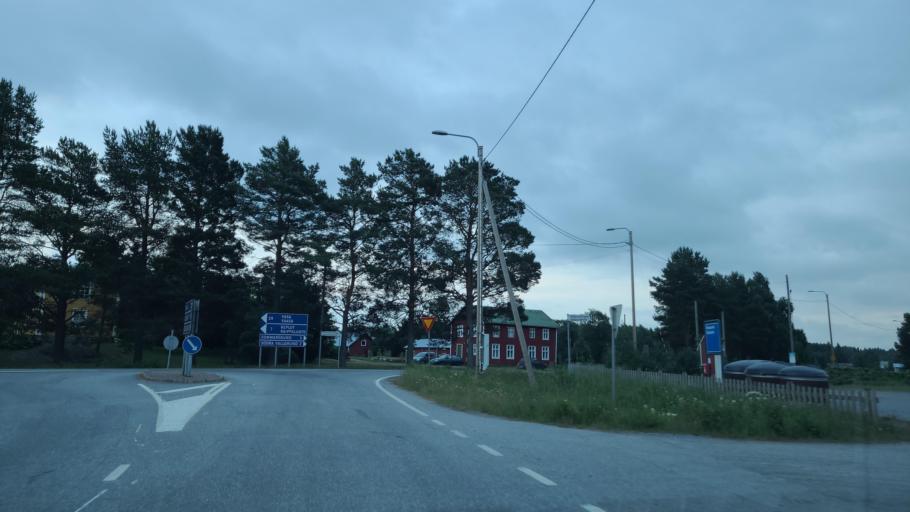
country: FI
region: Ostrobothnia
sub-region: Vaasa
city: Replot
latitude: 63.1962
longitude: 21.3051
